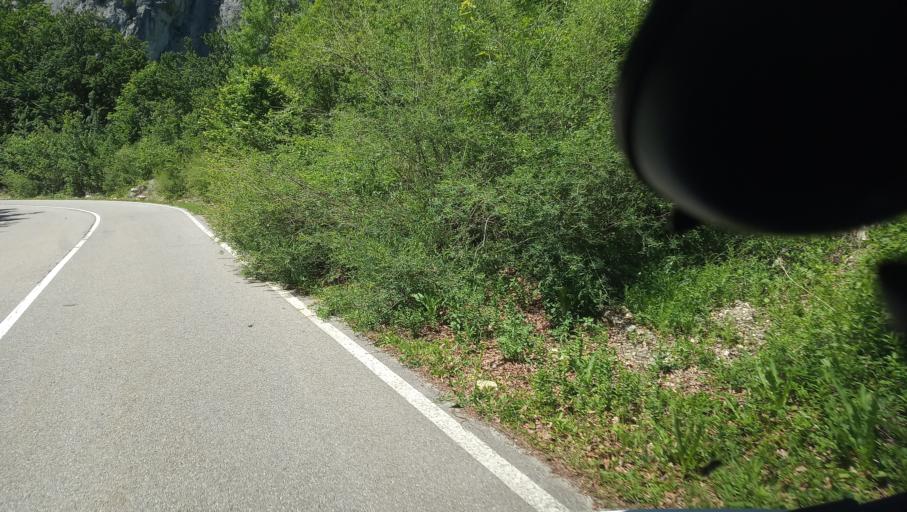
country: RO
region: Mehedinti
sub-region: Comuna Isverna
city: Isverna
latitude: 45.0550
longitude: 22.6024
